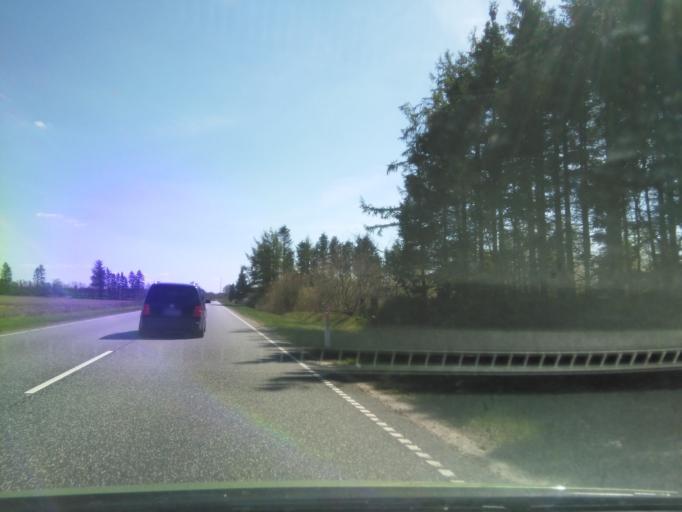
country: DK
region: Central Jutland
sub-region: Ikast-Brande Kommune
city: Bording Kirkeby
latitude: 56.2408
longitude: 9.3226
